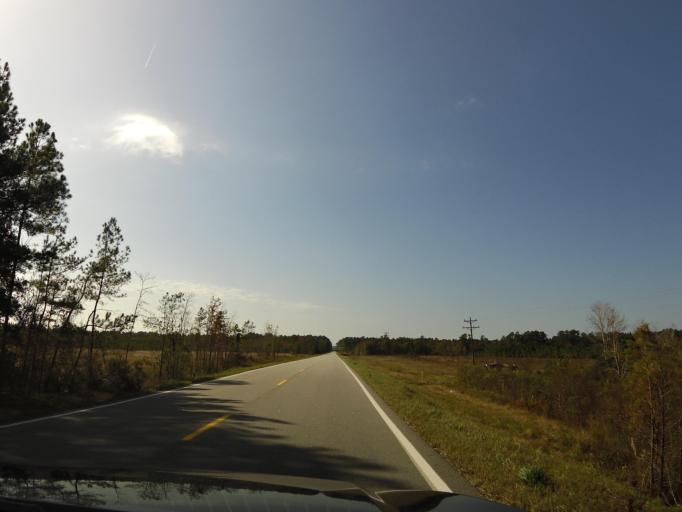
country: US
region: Georgia
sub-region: Charlton County
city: Folkston
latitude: 30.8085
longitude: -82.0230
